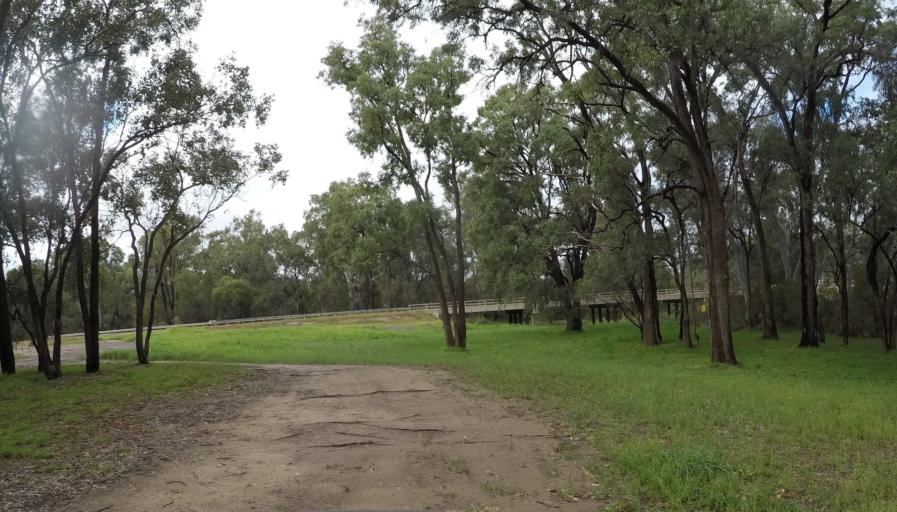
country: AU
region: Queensland
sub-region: Maranoa
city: Roma
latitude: -26.6109
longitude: 149.3898
